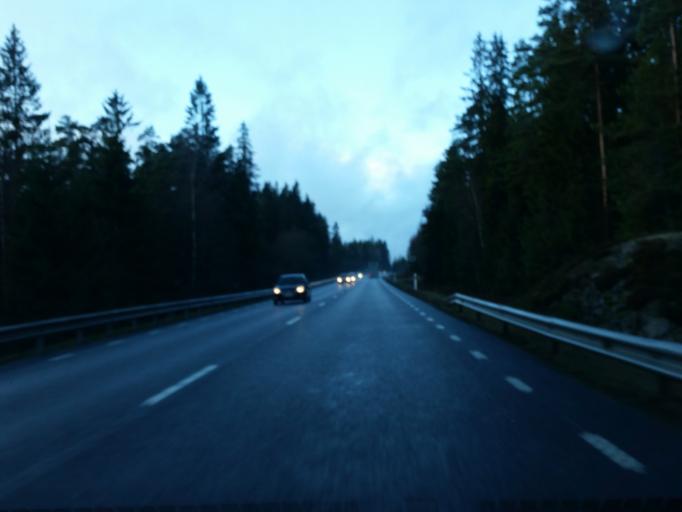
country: SE
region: Joenkoeping
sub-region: Gislaveds Kommun
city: Gislaved
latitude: 57.3281
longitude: 13.5334
